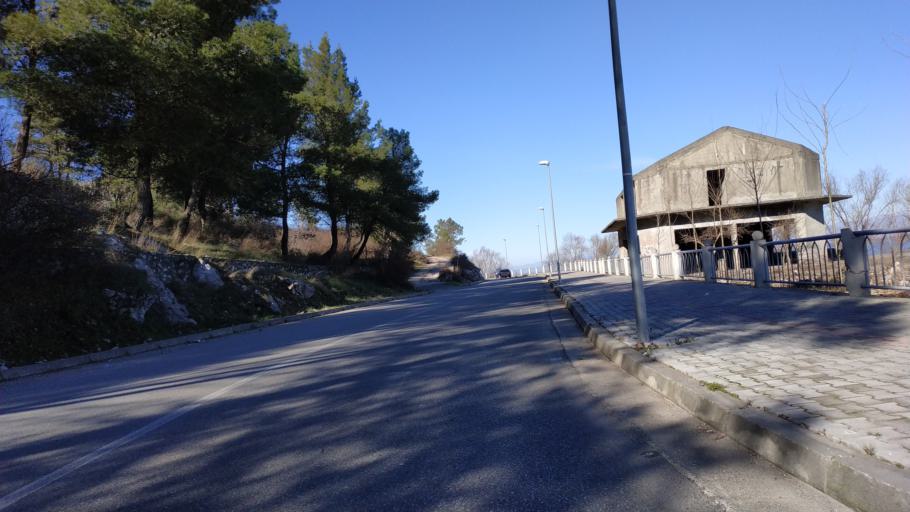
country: AL
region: Shkoder
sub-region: Rrethi i Shkodres
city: Berdica e Madhe
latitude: 42.0561
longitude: 19.4672
